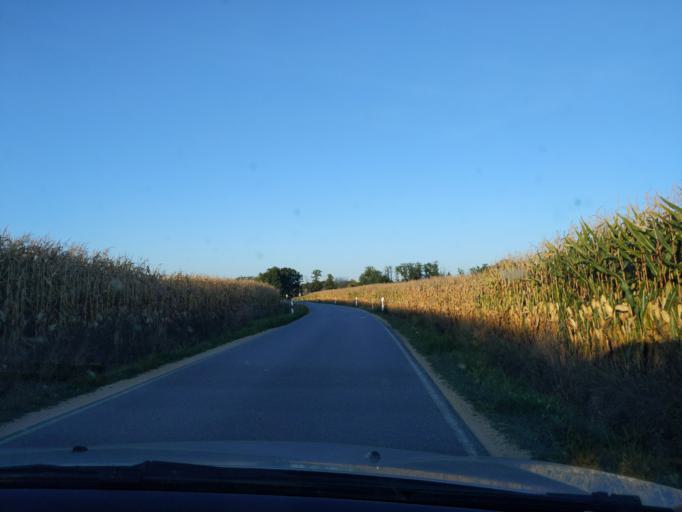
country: DE
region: Saxony
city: Guttau
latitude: 51.2648
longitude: 14.5641
